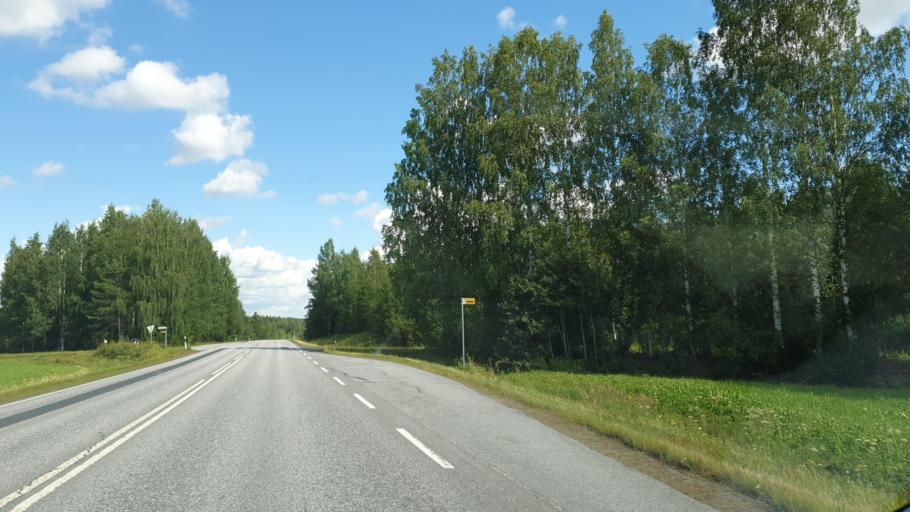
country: FI
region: Northern Savo
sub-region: Ylae-Savo
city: Sonkajaervi
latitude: 63.7516
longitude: 27.3871
